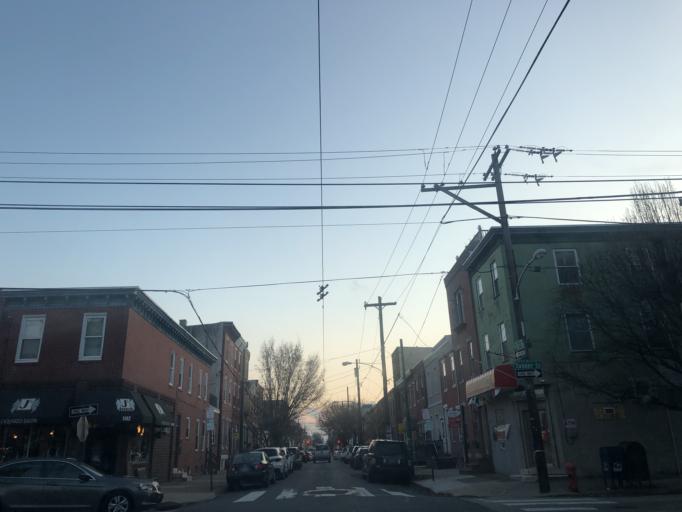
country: US
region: Pennsylvania
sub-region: Philadelphia County
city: Philadelphia
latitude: 39.9302
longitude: -75.1646
